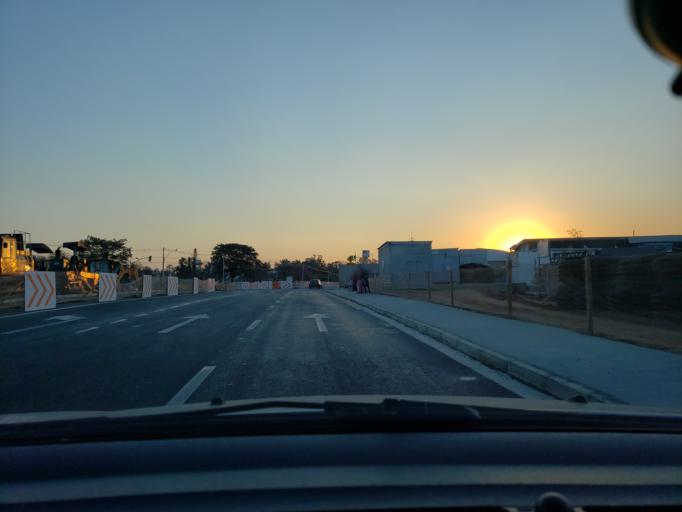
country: BR
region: Sao Paulo
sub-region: Campinas
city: Campinas
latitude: -22.9414
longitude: -47.1470
